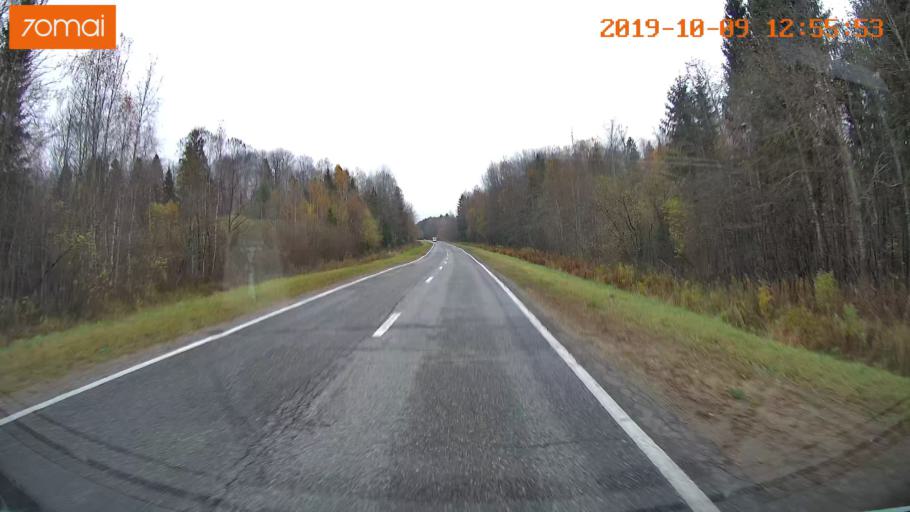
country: RU
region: Jaroslavl
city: Prechistoye
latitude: 58.3970
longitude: 40.4044
